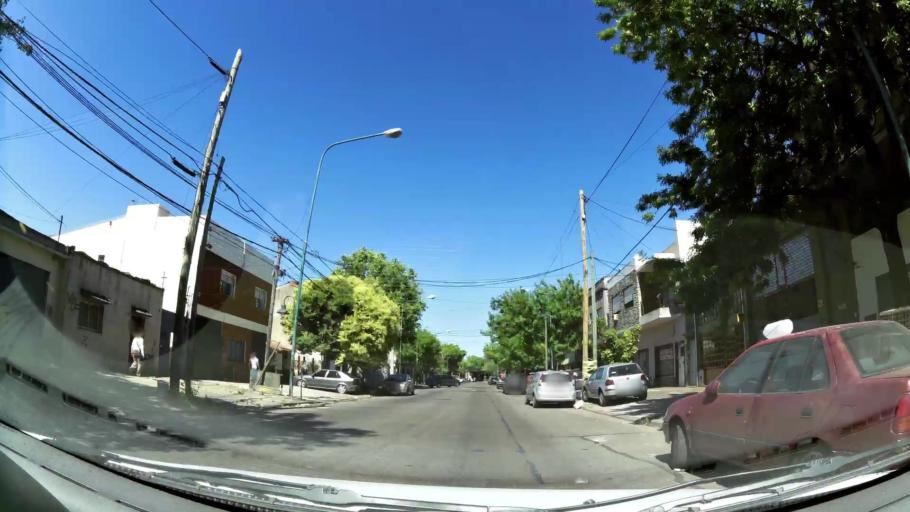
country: AR
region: Buenos Aires
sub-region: Partido de Vicente Lopez
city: Olivos
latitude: -34.5237
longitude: -58.5260
